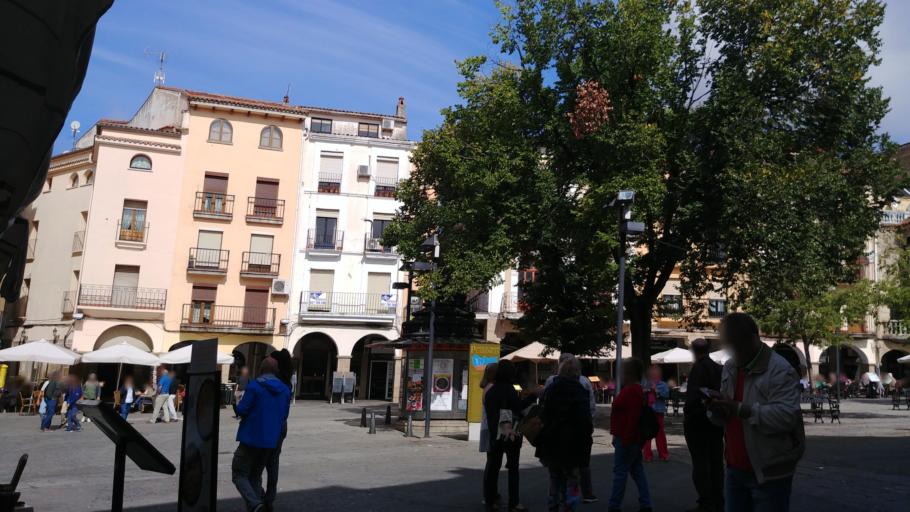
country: ES
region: Extremadura
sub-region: Provincia de Caceres
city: Plasencia
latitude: 40.0295
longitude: -6.0905
